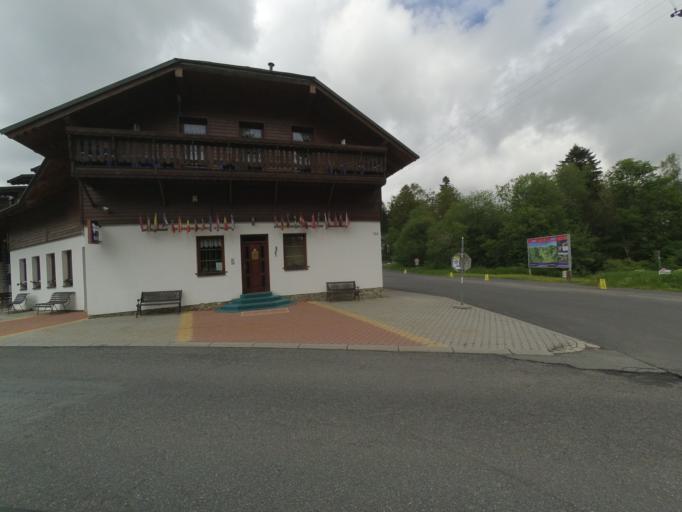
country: CZ
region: Plzensky
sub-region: Okres Klatovy
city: Zelezna Ruda
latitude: 49.1728
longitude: 13.2256
